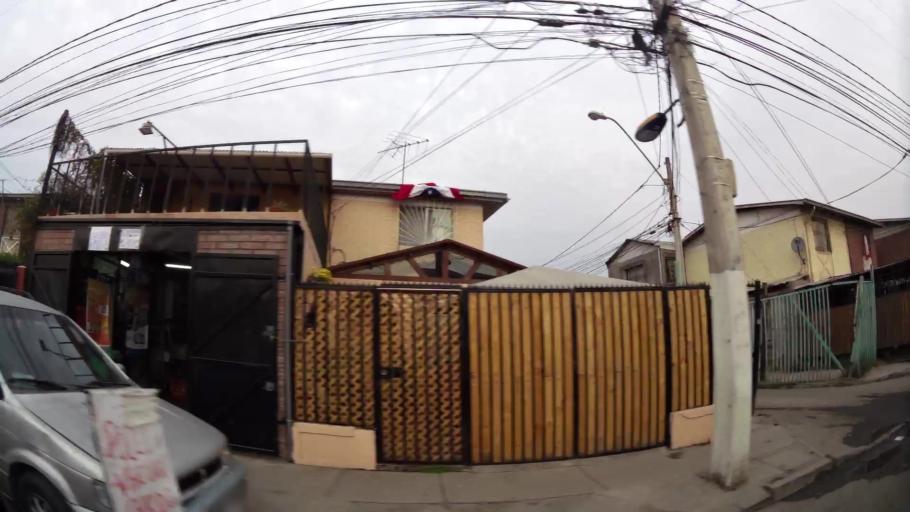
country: CL
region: Santiago Metropolitan
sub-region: Provincia de Santiago
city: Lo Prado
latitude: -33.5187
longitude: -70.7963
